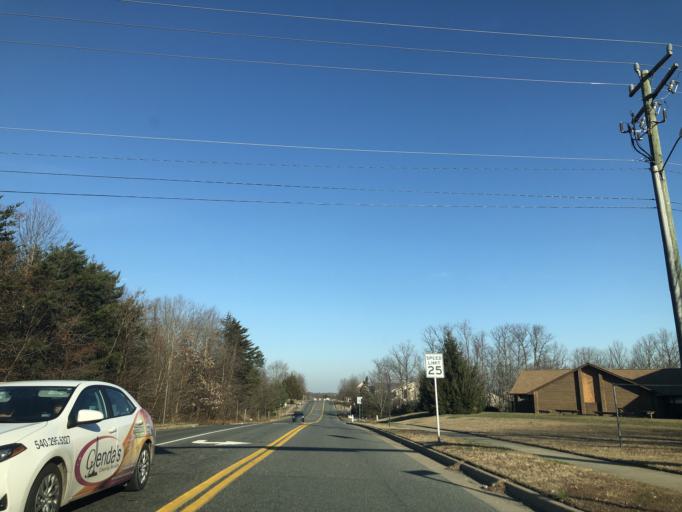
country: US
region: Virginia
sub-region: Stafford County
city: Stafford
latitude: 38.4207
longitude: -77.4146
